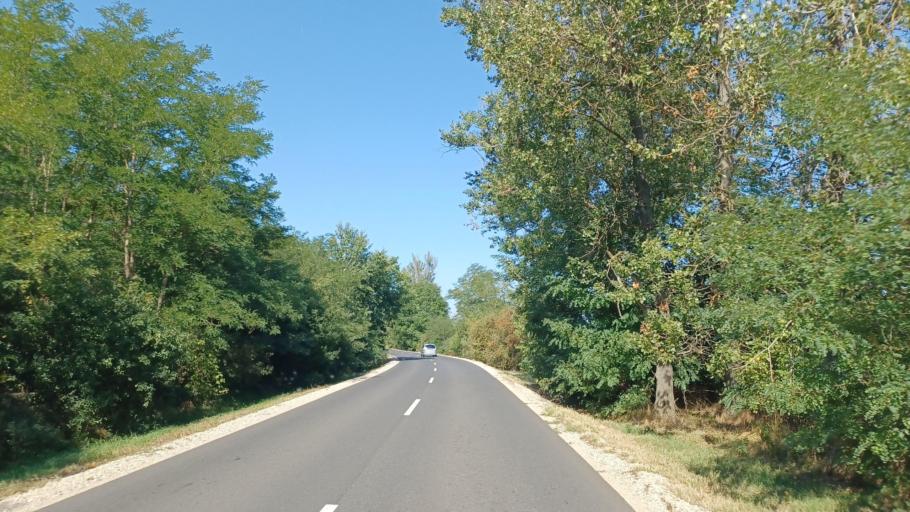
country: HU
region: Fejer
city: Alap
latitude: 46.7456
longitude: 18.6920
